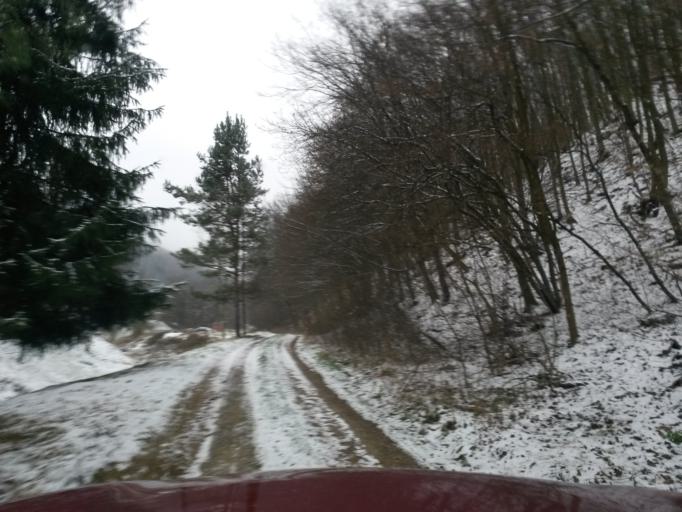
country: SK
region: Presovsky
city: Sabinov
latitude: 48.9672
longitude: 21.0900
